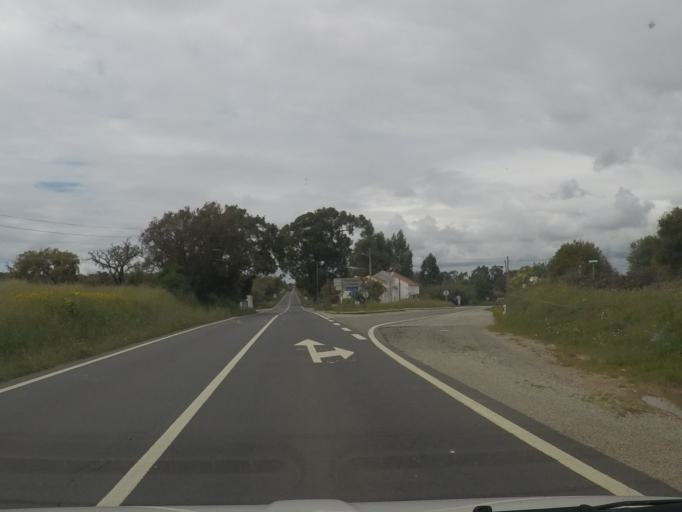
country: PT
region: Setubal
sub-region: Santiago do Cacem
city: Cercal
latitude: 37.8507
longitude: -8.7103
